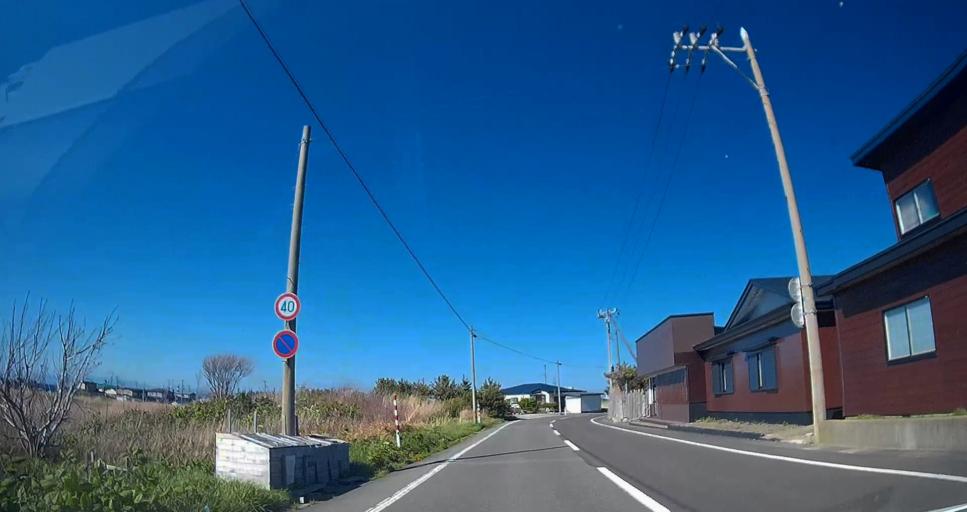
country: JP
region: Hokkaido
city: Hakodate
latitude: 41.5433
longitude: 140.9130
